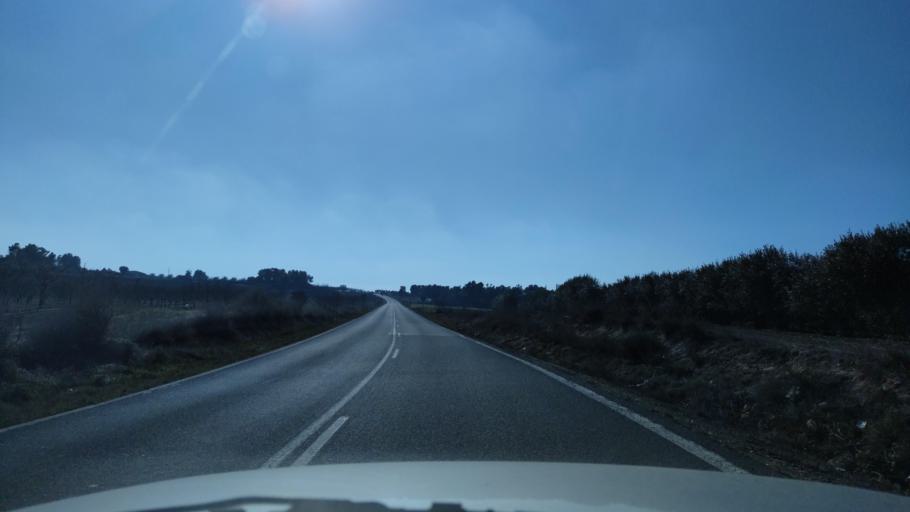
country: ES
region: Catalonia
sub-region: Provincia de Lleida
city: Maials
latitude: 41.3543
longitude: 0.4707
